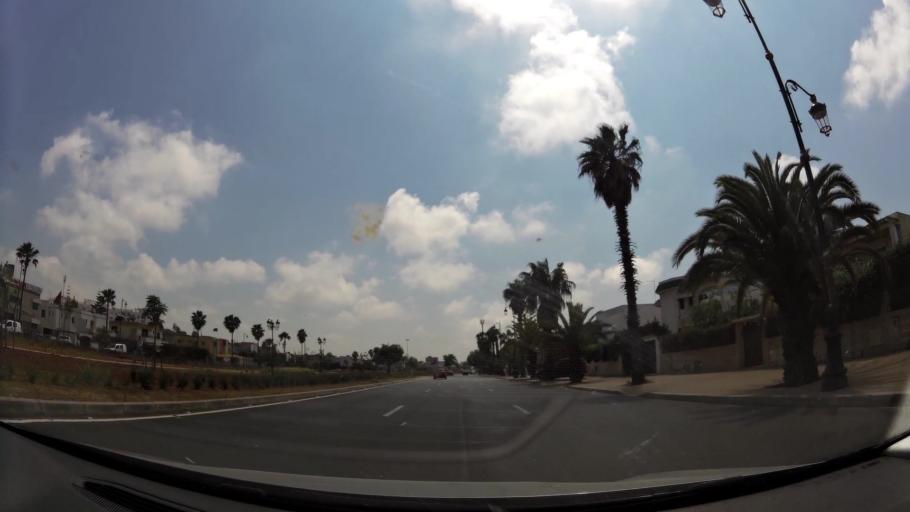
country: MA
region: Rabat-Sale-Zemmour-Zaer
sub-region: Skhirate-Temara
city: Temara
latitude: 33.9622
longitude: -6.8738
